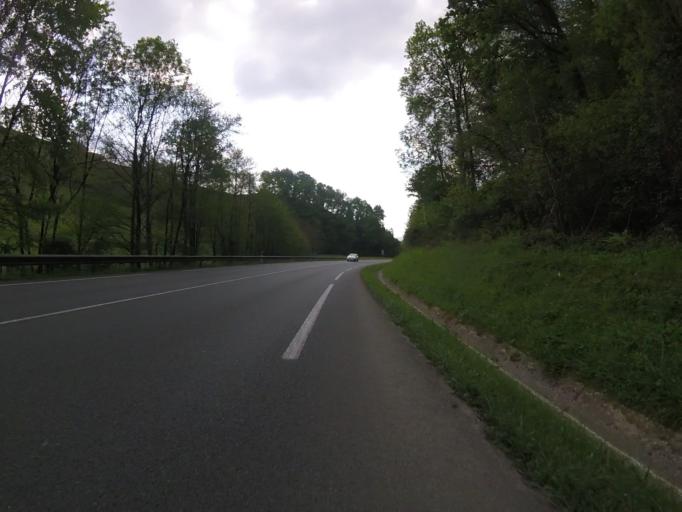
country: ES
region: Basque Country
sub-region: Provincia de Guipuzcoa
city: Azkoitia
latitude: 43.1852
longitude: -2.3249
